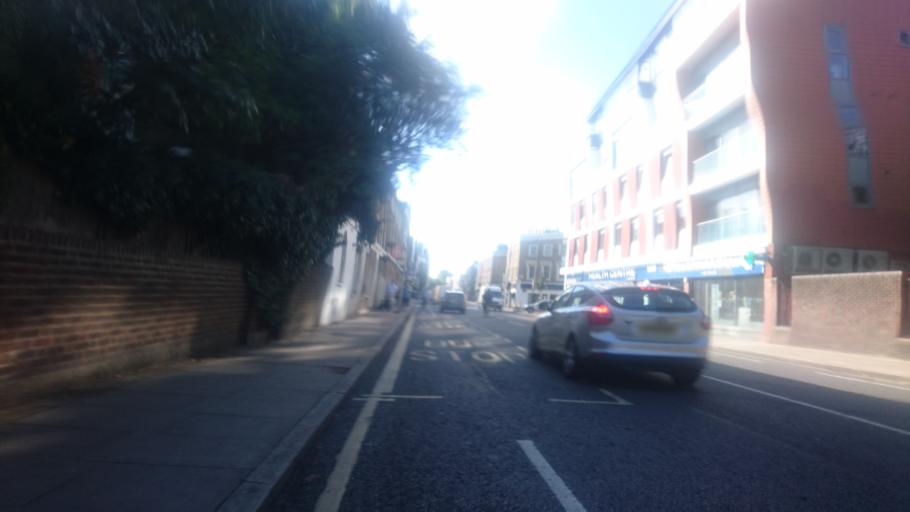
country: GB
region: England
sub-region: Greater London
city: Islington
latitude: 51.5385
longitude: -0.0924
